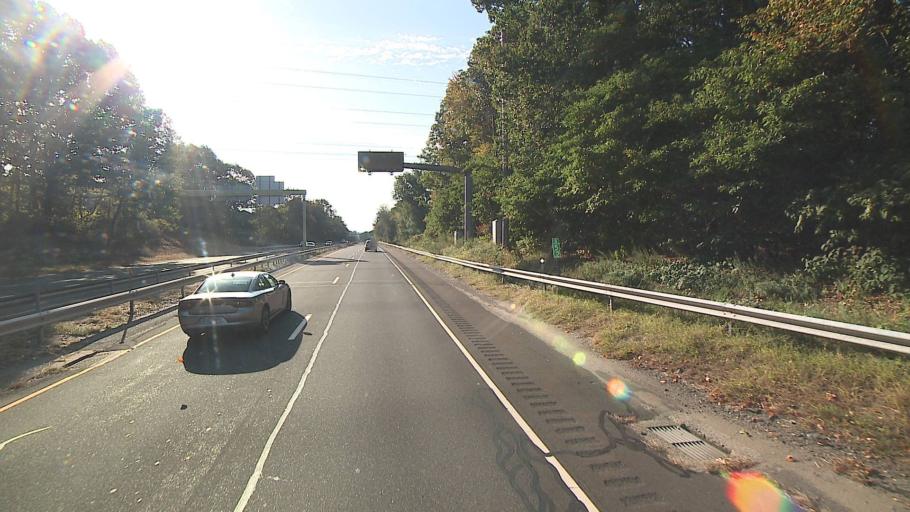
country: US
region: Connecticut
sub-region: New Haven County
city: City of Milford (balance)
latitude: 41.2421
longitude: -73.0803
